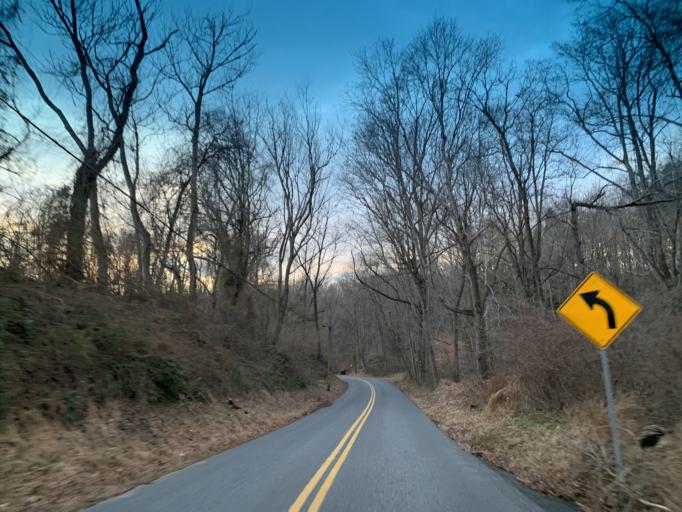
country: US
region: Maryland
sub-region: Harford County
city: Bel Air North
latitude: 39.6278
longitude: -76.3083
